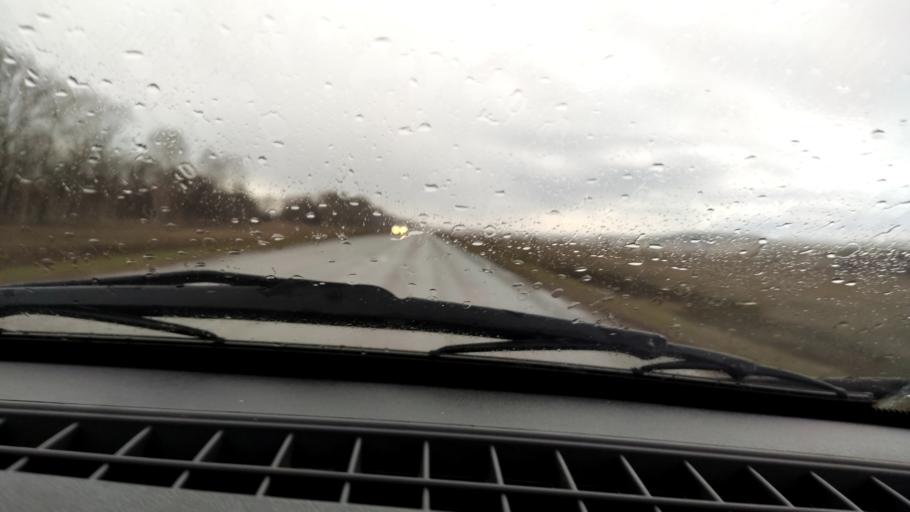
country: RU
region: Bashkortostan
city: Chekmagush
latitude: 55.1230
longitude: 54.7244
